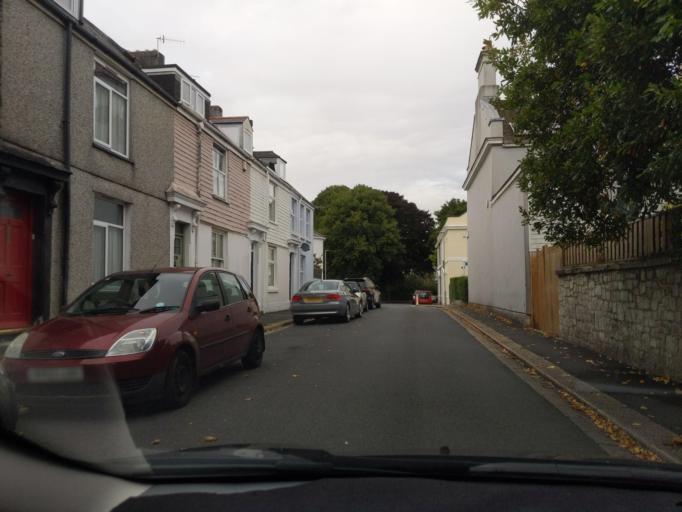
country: GB
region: England
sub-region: Cornwall
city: Millbrook
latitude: 50.3749
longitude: -4.1647
